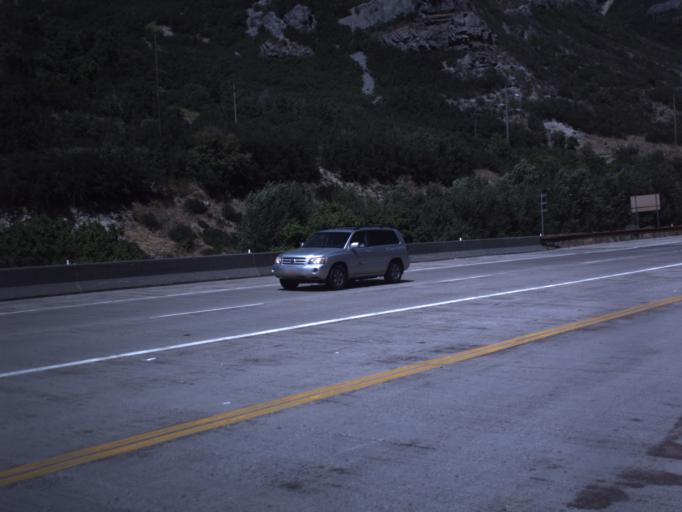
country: US
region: Utah
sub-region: Utah County
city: Orem
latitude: 40.3376
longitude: -111.6103
